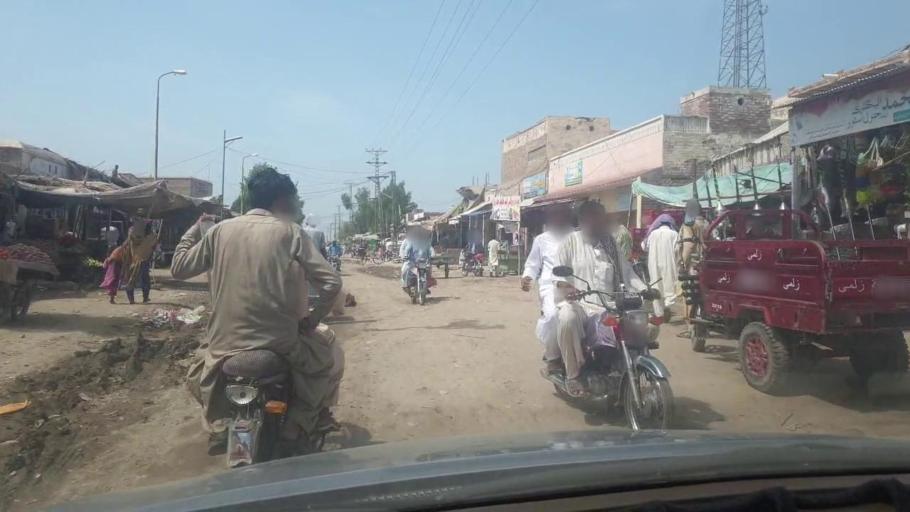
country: PK
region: Sindh
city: Gambat
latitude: 27.3004
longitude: 68.6112
